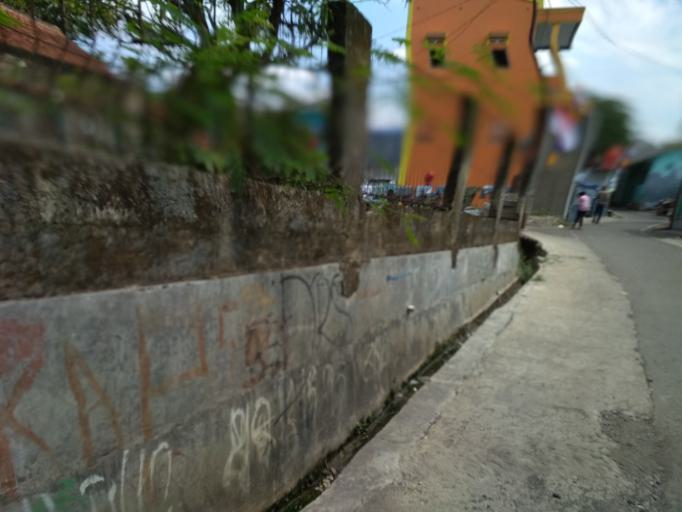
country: ID
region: West Java
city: Ciampea
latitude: -6.5630
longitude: 106.7468
